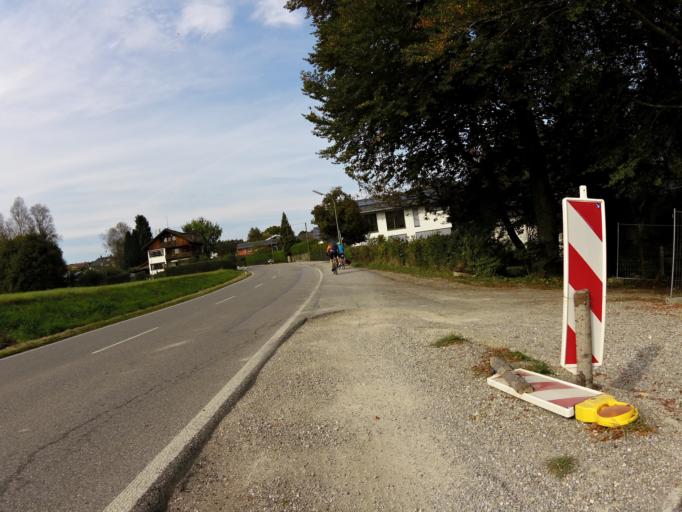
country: DE
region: Bavaria
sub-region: Upper Bavaria
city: Tutzing
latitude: 47.8879
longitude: 11.2683
